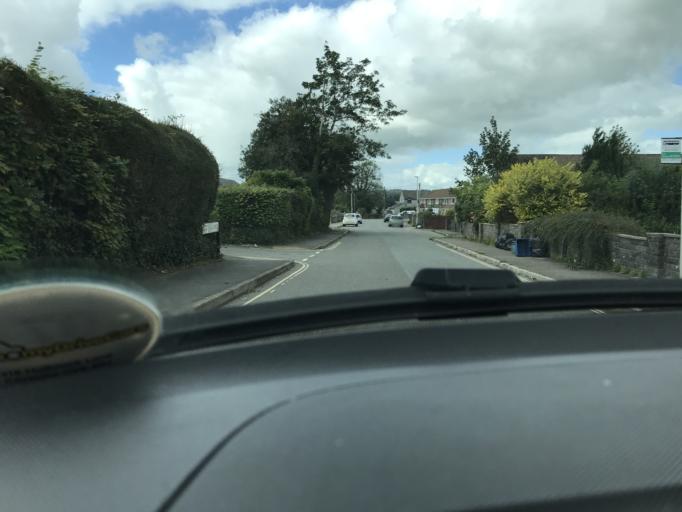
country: GB
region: England
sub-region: Devon
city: Tavistock
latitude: 50.5478
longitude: -4.1315
